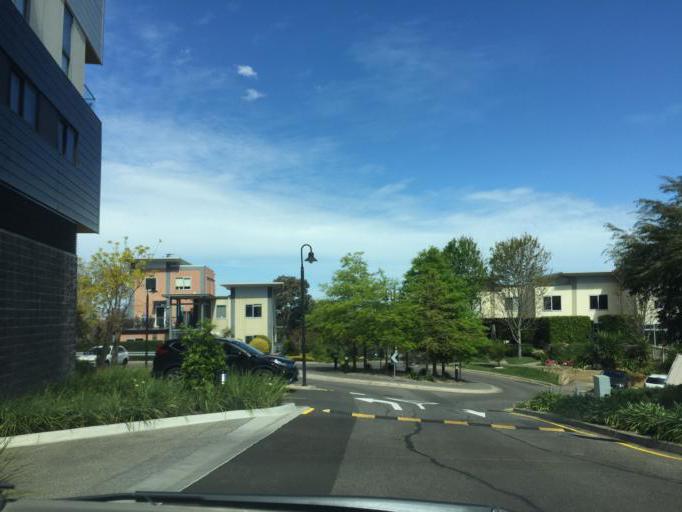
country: AU
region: Victoria
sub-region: Maribyrnong
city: Maribyrnong
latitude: -37.7754
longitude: 144.8922
